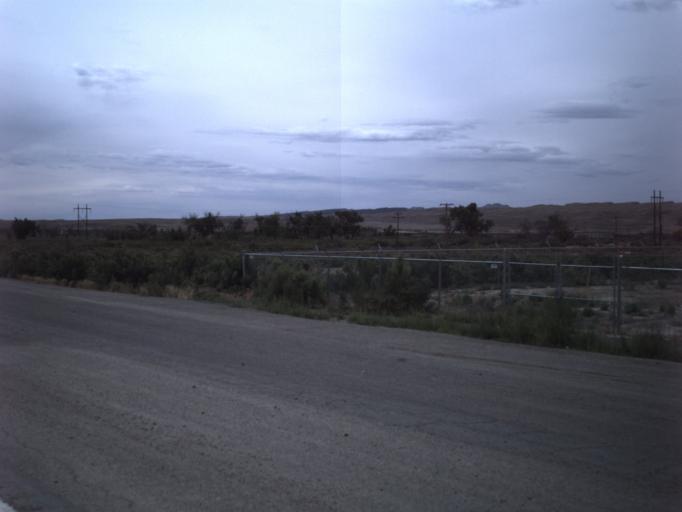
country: US
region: Utah
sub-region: Carbon County
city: East Carbon City
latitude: 39.2666
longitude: -110.3440
